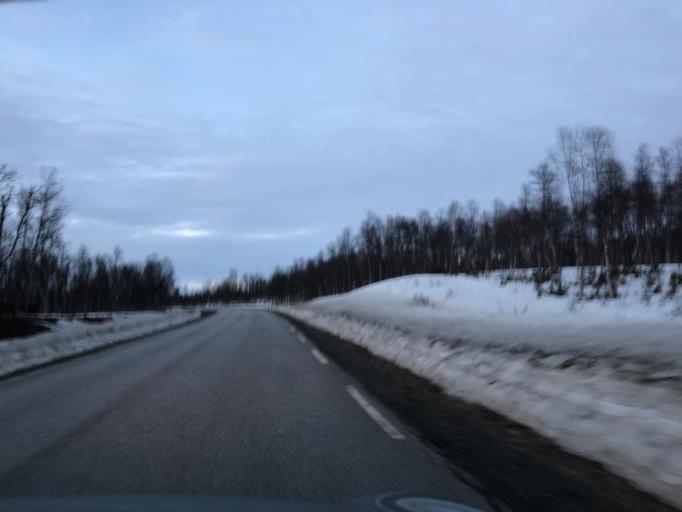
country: NO
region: Sor-Trondelag
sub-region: Tydal
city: Aas
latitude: 62.6948
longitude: 11.7814
